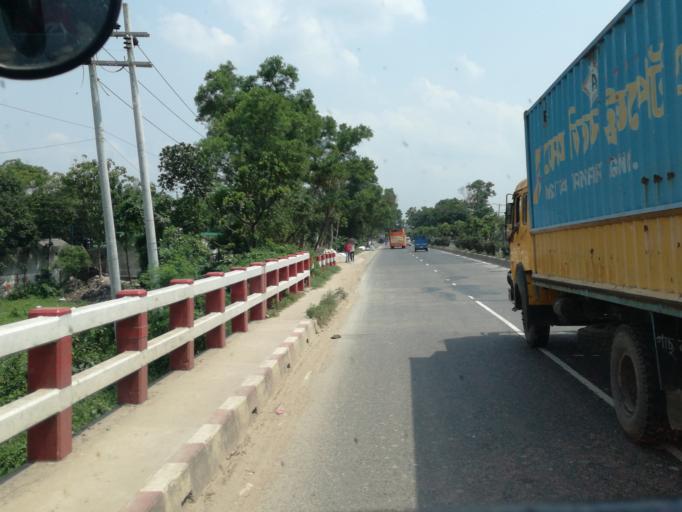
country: BD
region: Dhaka
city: Azimpur
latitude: 23.8008
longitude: 90.2629
